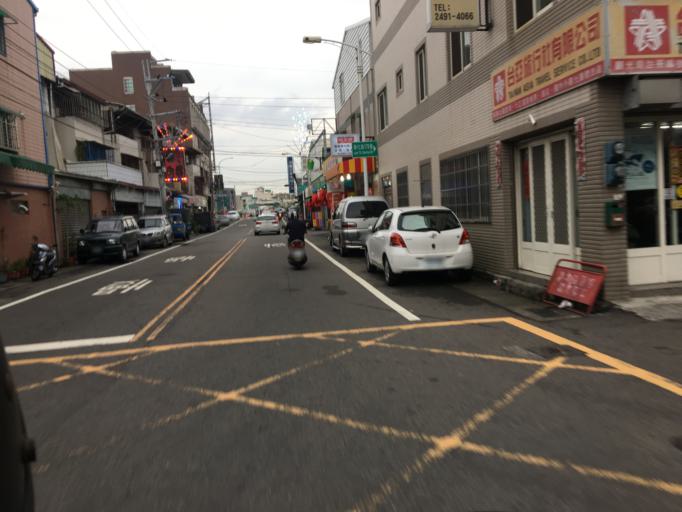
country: TW
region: Taiwan
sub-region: Taichung City
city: Taichung
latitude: 24.0993
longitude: 120.7019
